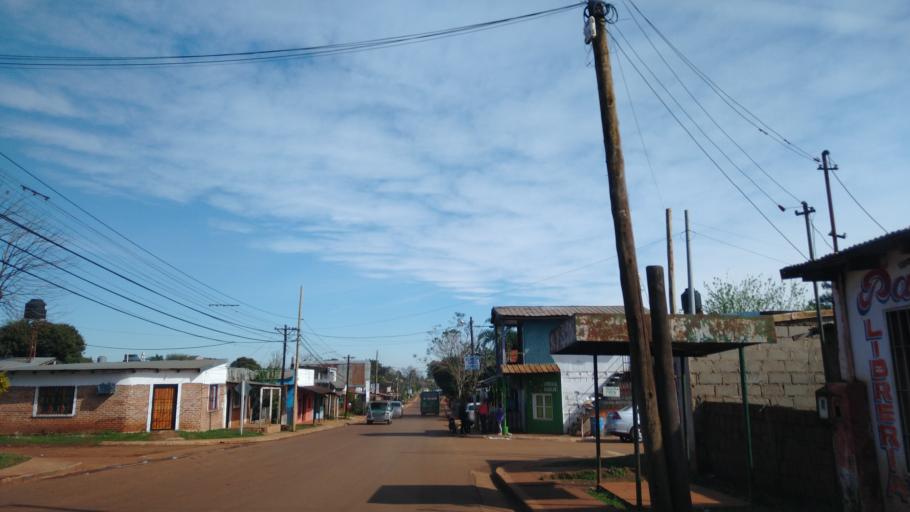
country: AR
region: Misiones
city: Garupa
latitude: -27.4660
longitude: -55.8596
